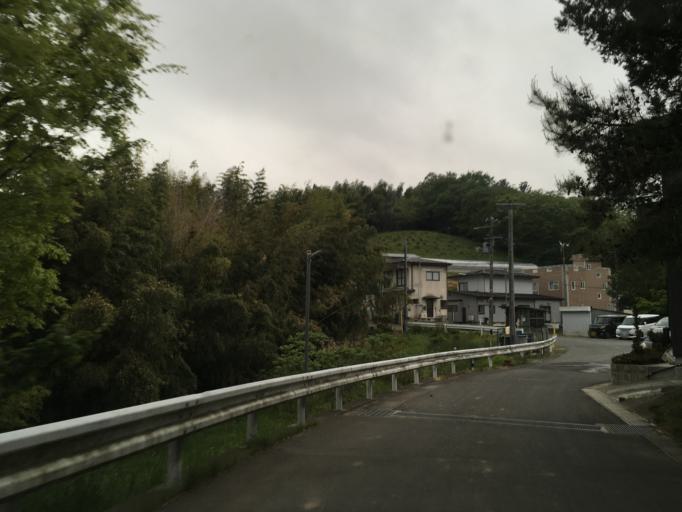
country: JP
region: Miyagi
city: Wakuya
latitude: 38.7077
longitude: 141.2850
